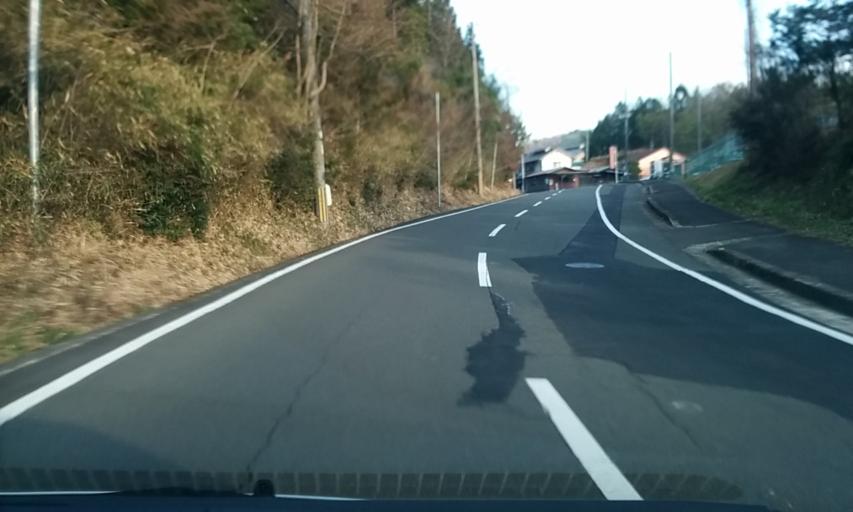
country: JP
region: Kyoto
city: Ayabe
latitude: 35.2880
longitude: 135.2451
